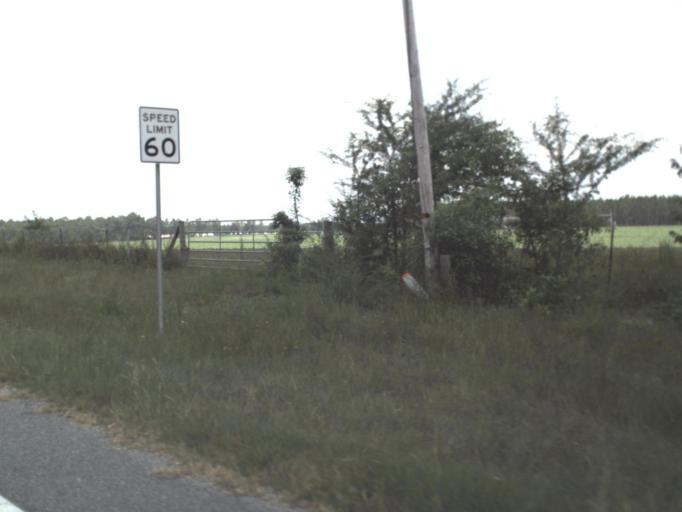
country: US
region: Florida
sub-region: Hamilton County
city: Jasper
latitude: 30.4901
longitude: -83.1359
